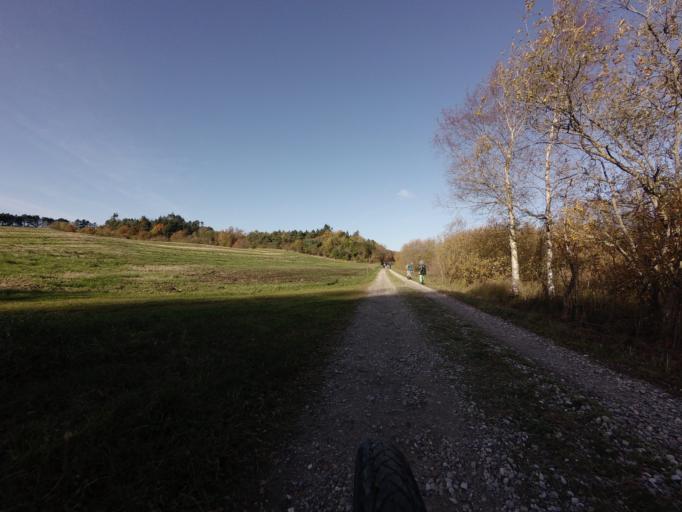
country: DK
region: Central Jutland
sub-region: Syddjurs Kommune
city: Ryomgard
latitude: 56.4411
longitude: 10.6227
